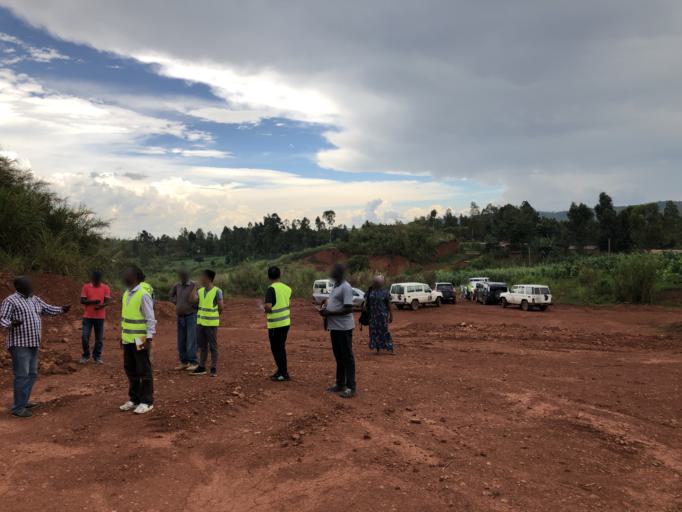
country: CD
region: Eastern Province
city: Bunia
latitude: 1.6975
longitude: 30.2829
